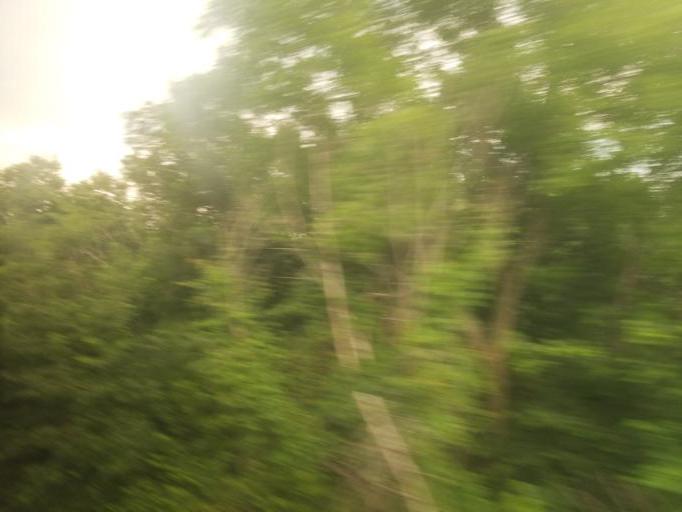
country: US
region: Illinois
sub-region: Bureau County
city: Princeton
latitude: 41.3912
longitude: -89.5087
